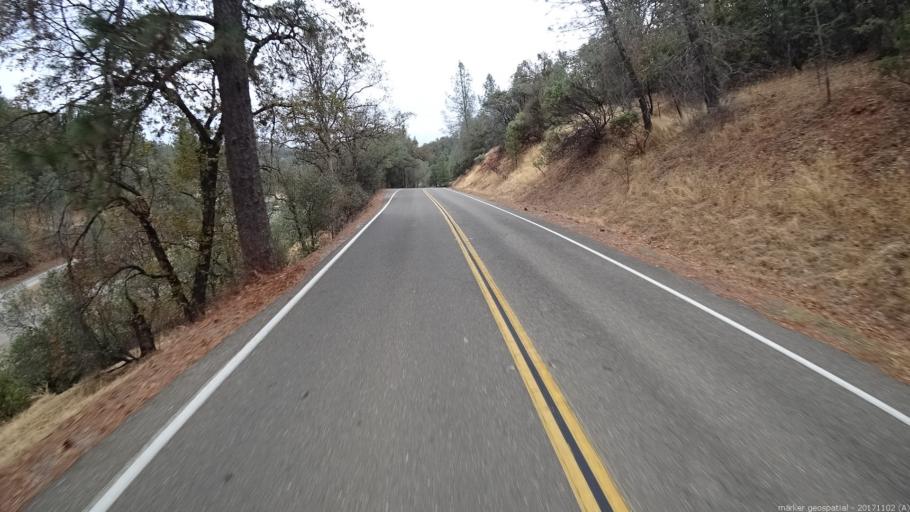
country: US
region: California
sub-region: Shasta County
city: Bella Vista
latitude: 40.7255
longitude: -122.2370
